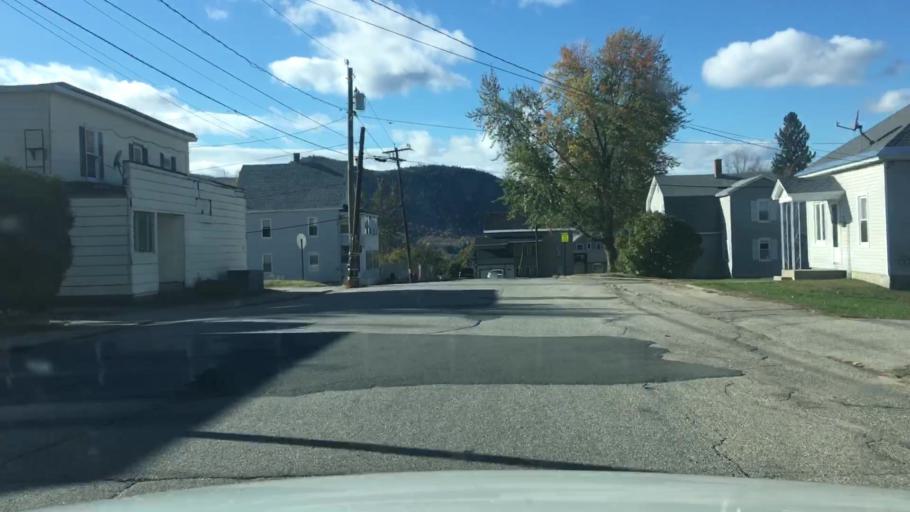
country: US
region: New Hampshire
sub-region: Coos County
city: Berlin
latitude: 44.4688
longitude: -71.1649
